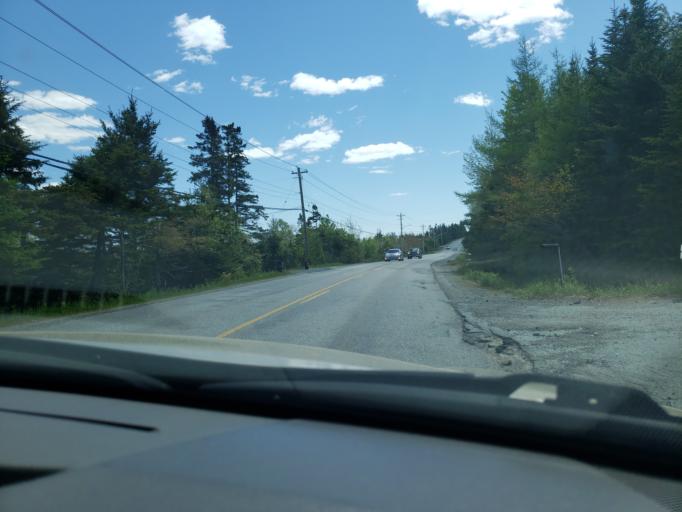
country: CA
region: Nova Scotia
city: Cole Harbour
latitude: 44.7302
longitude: -63.3071
